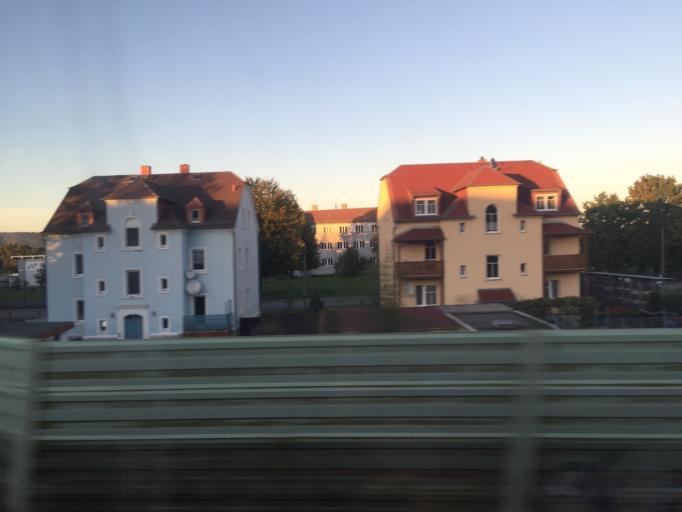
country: DE
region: Saxony
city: Heidenau
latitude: 50.9666
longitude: 13.8833
